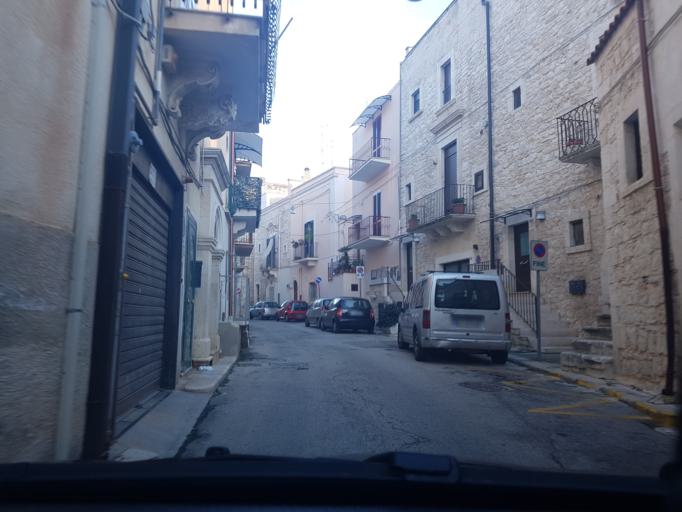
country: IT
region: Apulia
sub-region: Provincia di Bari
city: Bitritto
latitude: 41.0406
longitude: 16.8253
